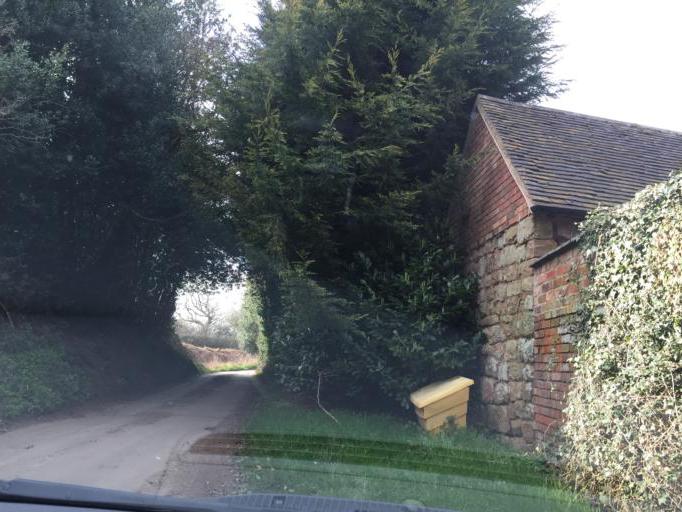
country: GB
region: England
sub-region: Solihull
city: Meriden
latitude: 52.4480
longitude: -1.5952
